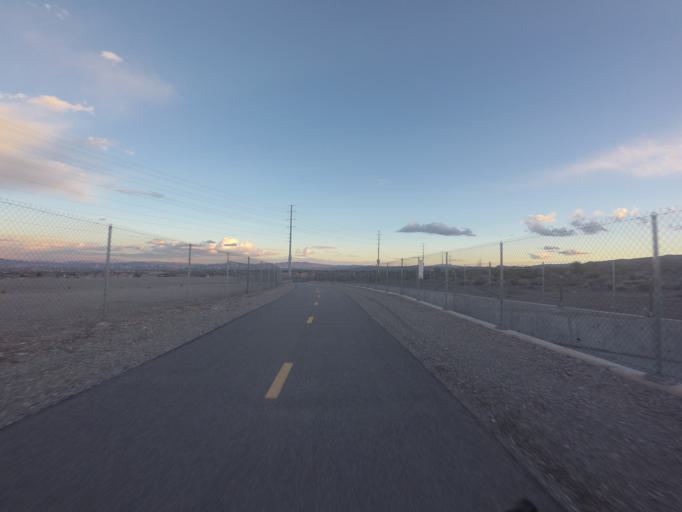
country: US
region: Nevada
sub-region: Clark County
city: Summerlin South
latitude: 36.1908
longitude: -115.3448
